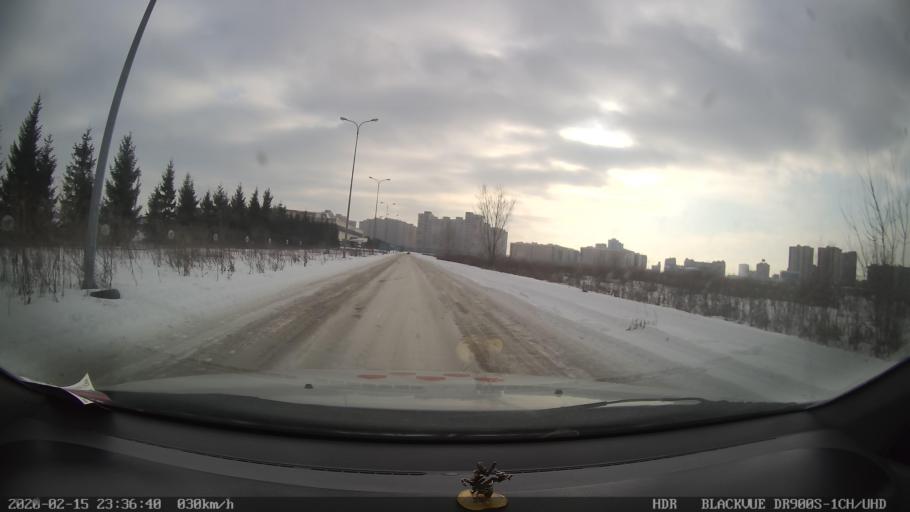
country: RU
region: Tatarstan
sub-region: Gorod Kazan'
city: Kazan
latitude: 55.7920
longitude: 49.1930
